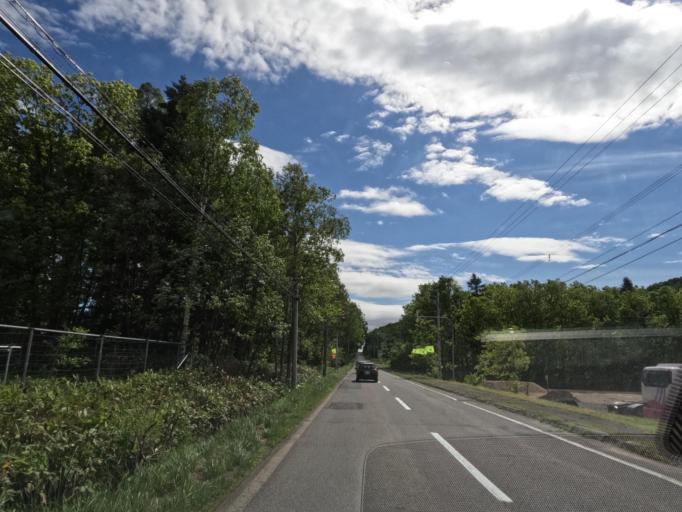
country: JP
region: Hokkaido
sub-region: Asahikawa-shi
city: Asahikawa
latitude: 43.8378
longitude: 142.5409
